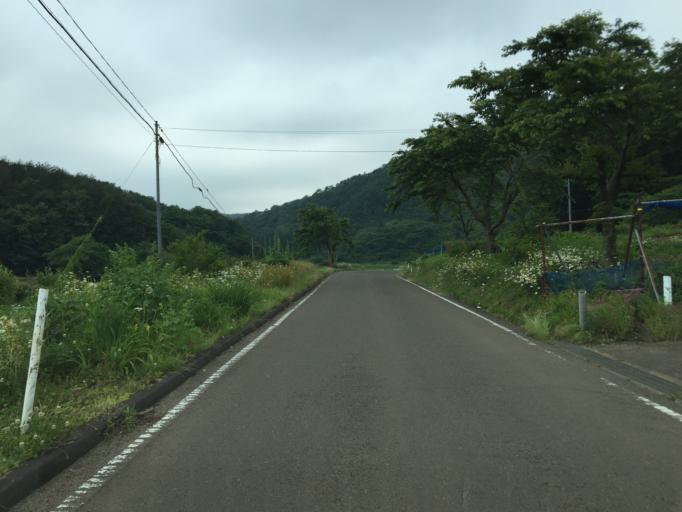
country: JP
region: Miyagi
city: Marumori
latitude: 37.7971
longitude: 140.7400
